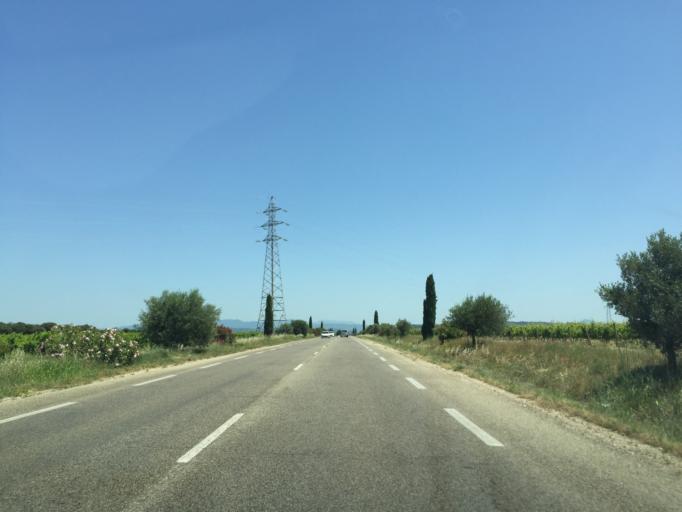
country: FR
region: Provence-Alpes-Cote d'Azur
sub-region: Departement du Vaucluse
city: Sainte-Cecile-les-Vignes
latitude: 44.2156
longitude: 4.8719
